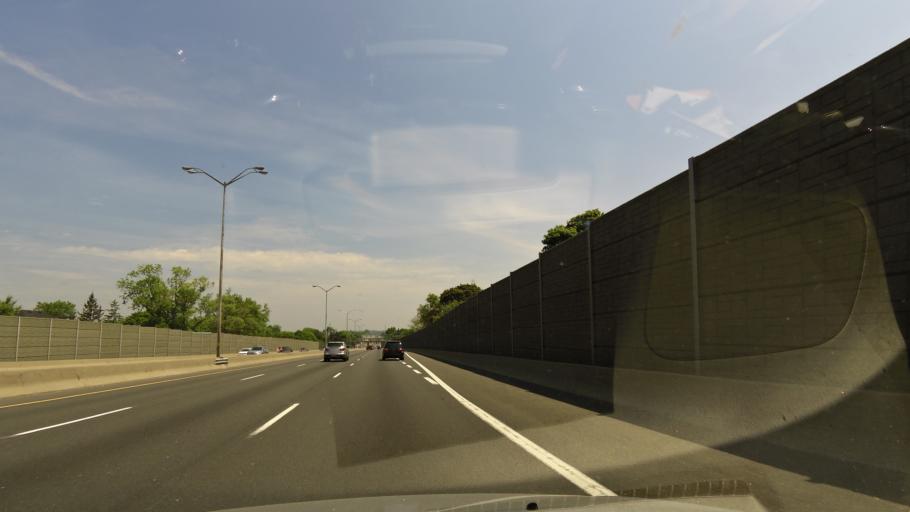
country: CA
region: Ontario
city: Oshawa
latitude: 43.8799
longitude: -78.8624
